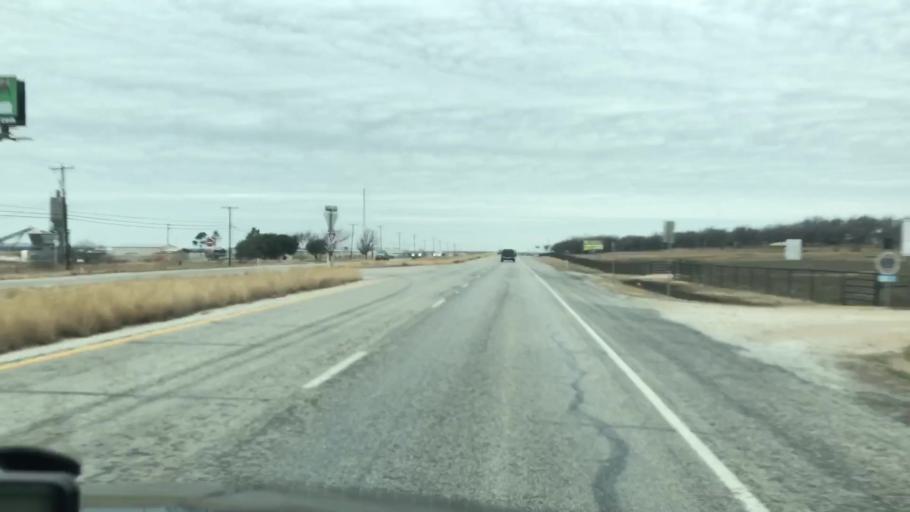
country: US
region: Texas
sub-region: Jack County
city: Jacksboro
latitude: 33.1929
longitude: -98.1402
